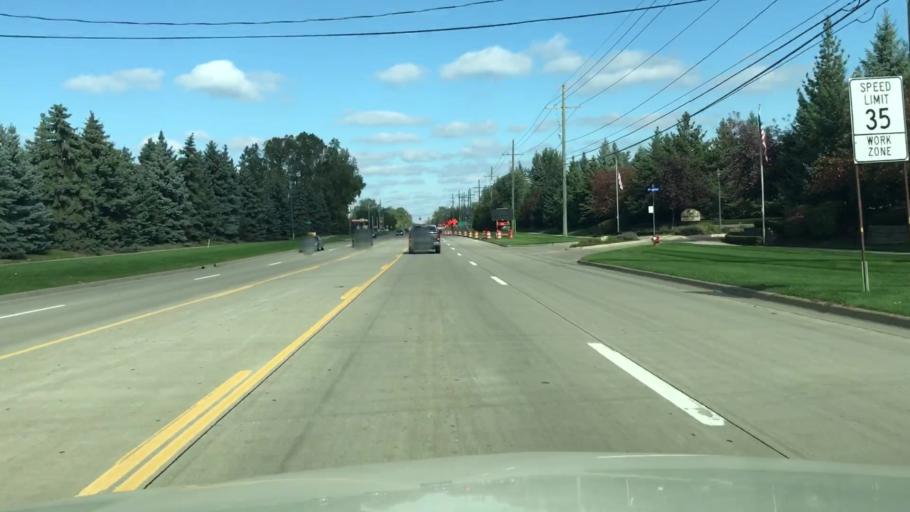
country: US
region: Michigan
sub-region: Macomb County
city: Sterling Heights
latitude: 42.5894
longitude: -83.0897
